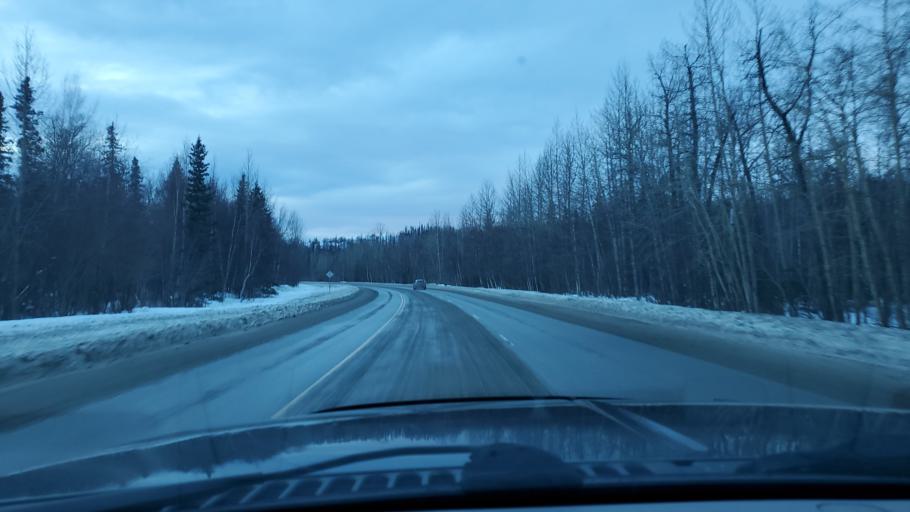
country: US
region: Alaska
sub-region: Matanuska-Susitna Borough
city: Lazy Mountain
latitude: 61.7085
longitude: -148.9390
